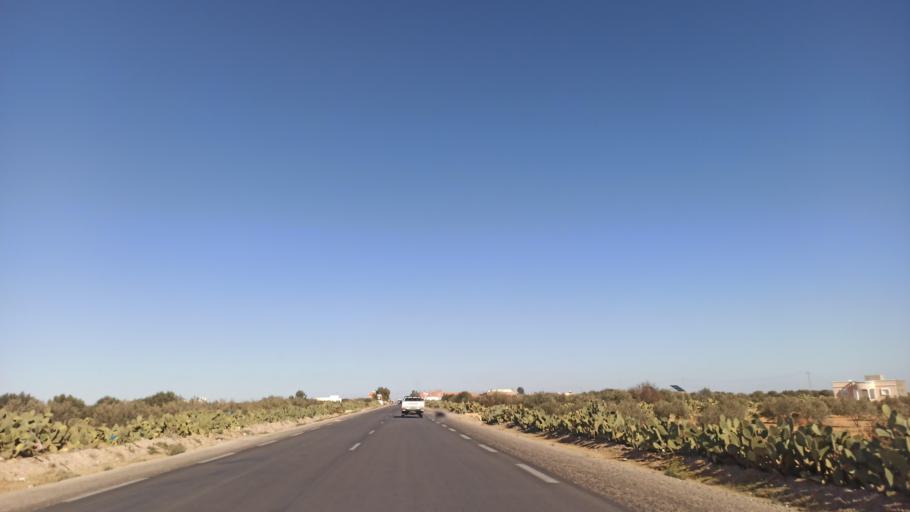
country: TN
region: Sidi Bu Zayd
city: Bi'r al Hufayy
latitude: 34.9669
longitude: 9.2263
